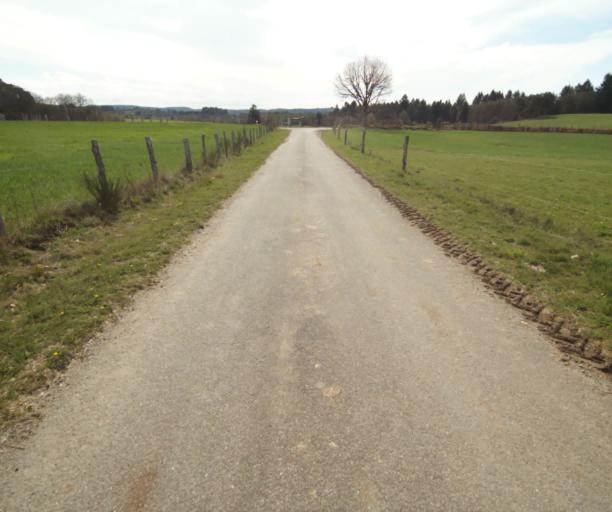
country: FR
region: Limousin
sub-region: Departement de la Correze
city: Correze
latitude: 45.3571
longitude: 1.9106
